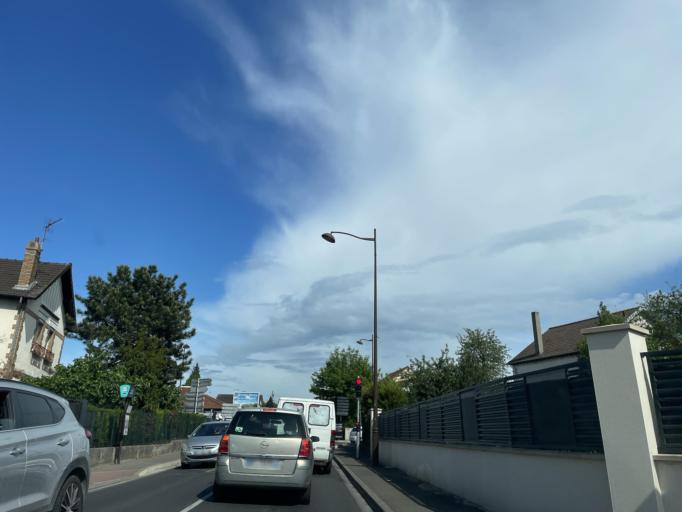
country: FR
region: Ile-de-France
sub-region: Departement du Val-d'Oise
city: Arnouville
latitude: 48.9862
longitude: 2.4148
